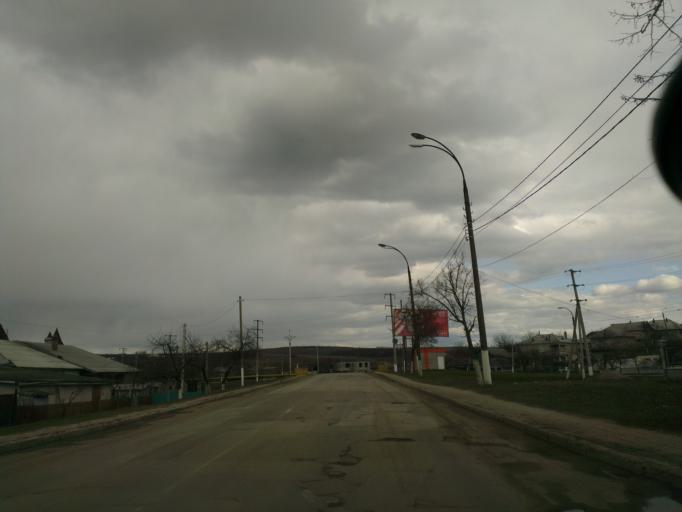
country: MD
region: Hincesti
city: Hincesti
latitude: 46.8198
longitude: 28.6007
